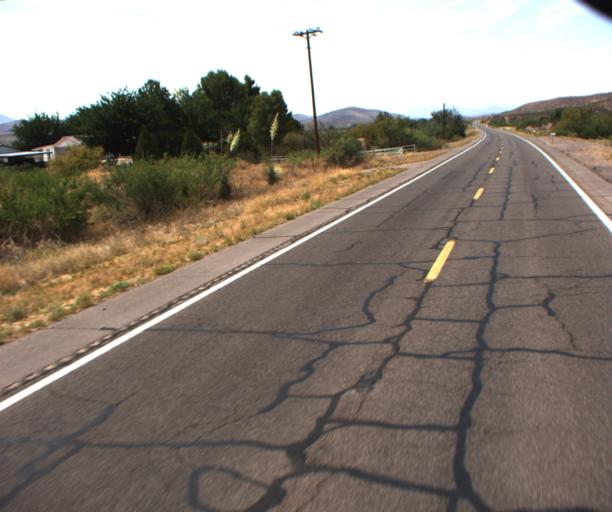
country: US
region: Arizona
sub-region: Greenlee County
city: Clifton
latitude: 32.8213
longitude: -109.1730
